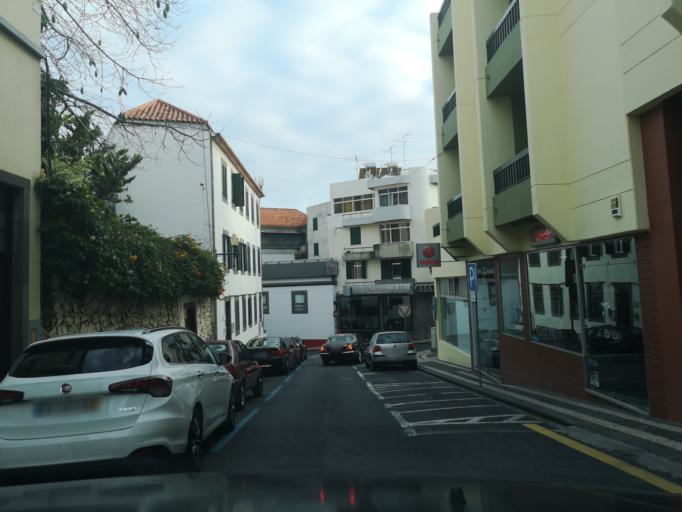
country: PT
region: Madeira
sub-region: Funchal
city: Funchal
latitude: 32.6494
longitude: -16.9154
